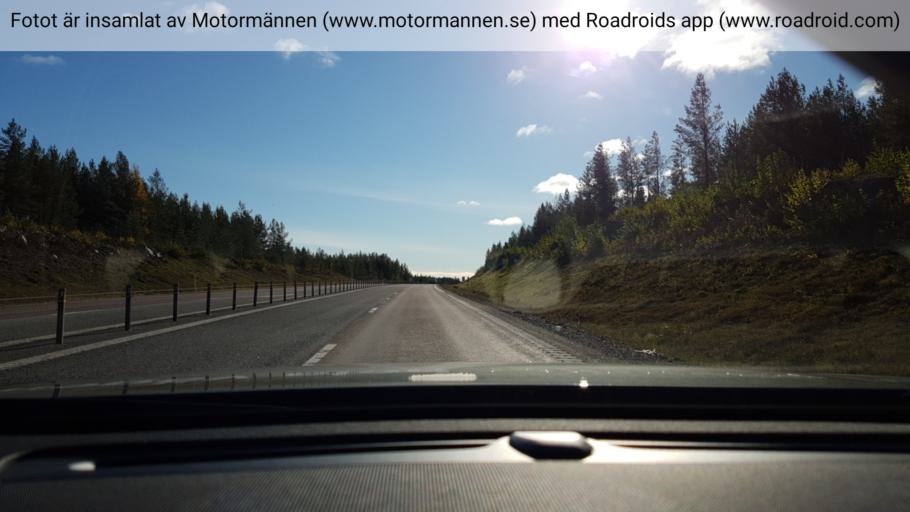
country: SE
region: Vaesterbotten
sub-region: Skelleftea Kommun
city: Soedra Bergsbyn
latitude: 64.6826
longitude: 21.0675
